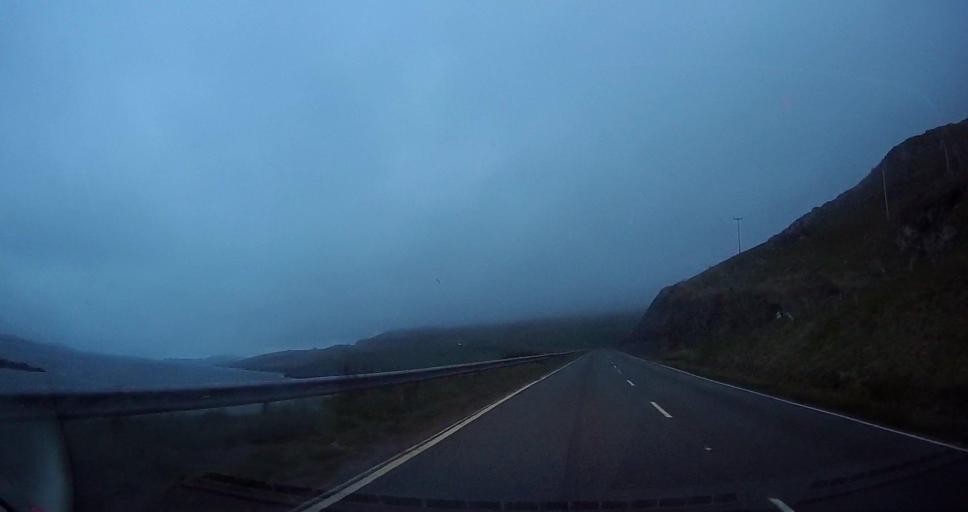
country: GB
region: Scotland
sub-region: Shetland Islands
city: Sandwick
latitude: 60.0325
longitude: -1.2338
